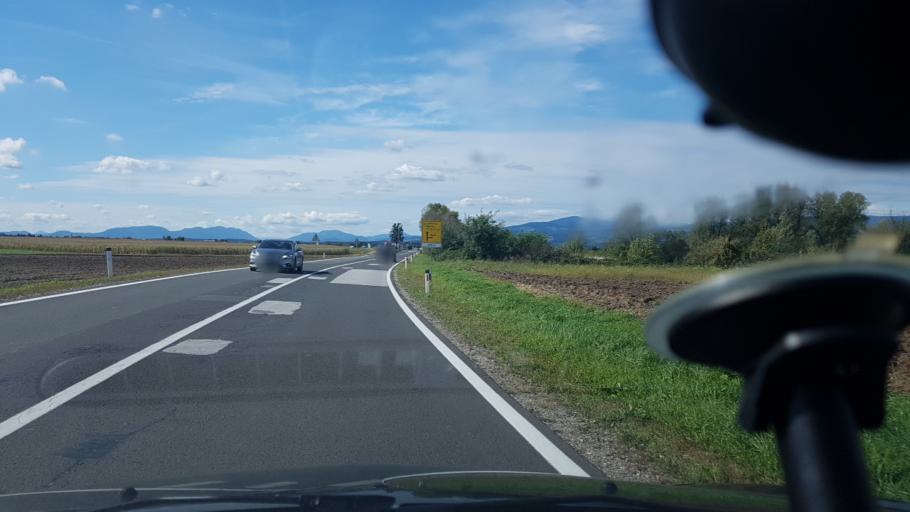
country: SI
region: Race-Fram
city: Race
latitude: 46.4085
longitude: 15.7162
